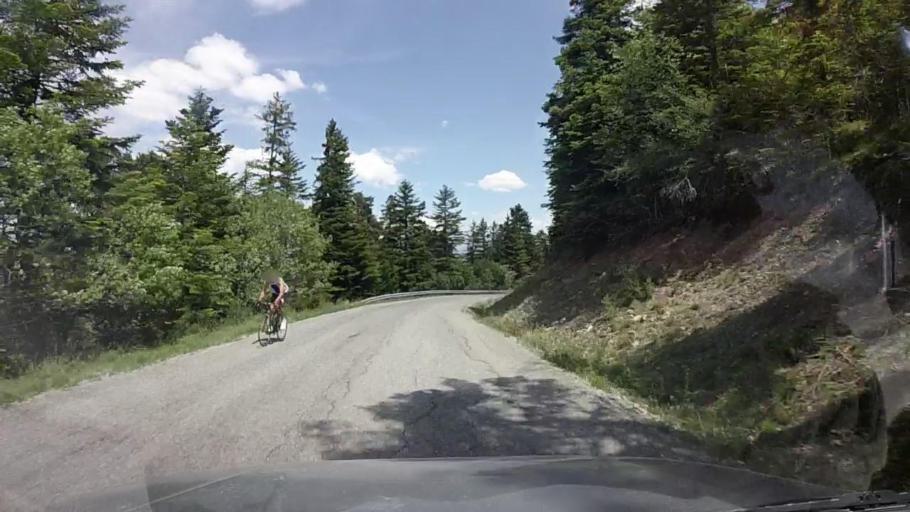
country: FR
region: Provence-Alpes-Cote d'Azur
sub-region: Departement des Alpes-de-Haute-Provence
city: Seyne-les-Alpes
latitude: 44.3515
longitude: 6.2952
